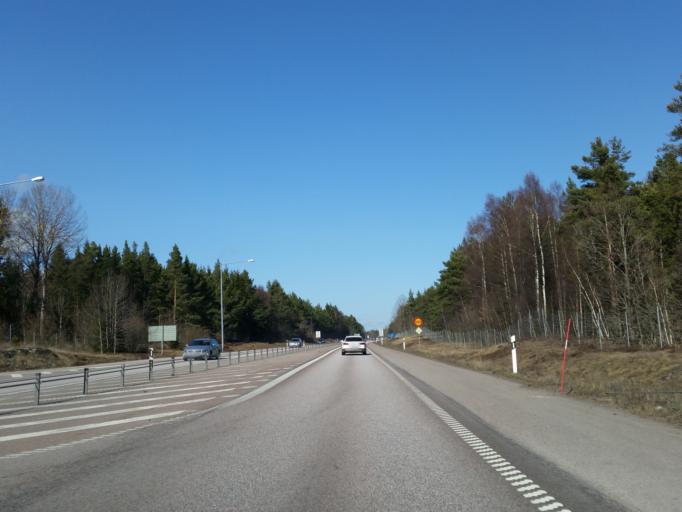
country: SE
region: Kalmar
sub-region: Oskarshamns Kommun
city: Paskallavik
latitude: 57.1968
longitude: 16.4381
